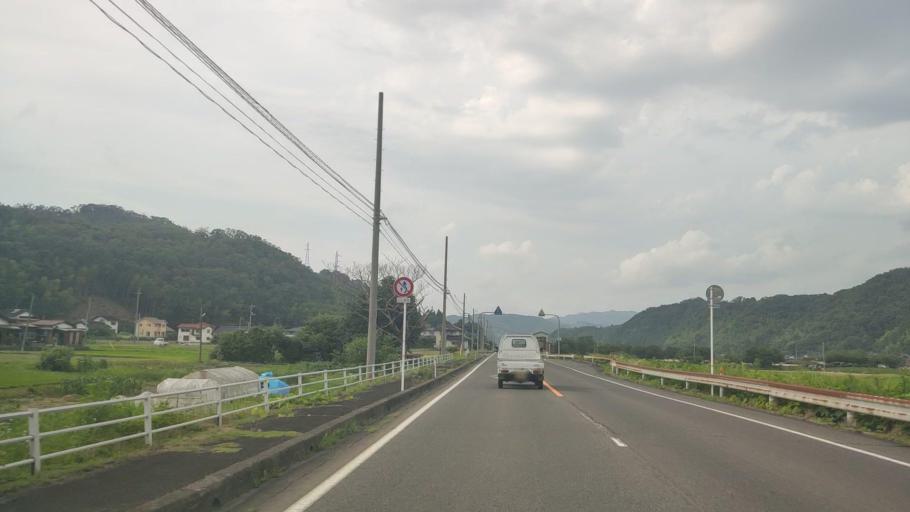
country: JP
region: Tottori
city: Kurayoshi
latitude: 35.3845
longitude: 133.8559
